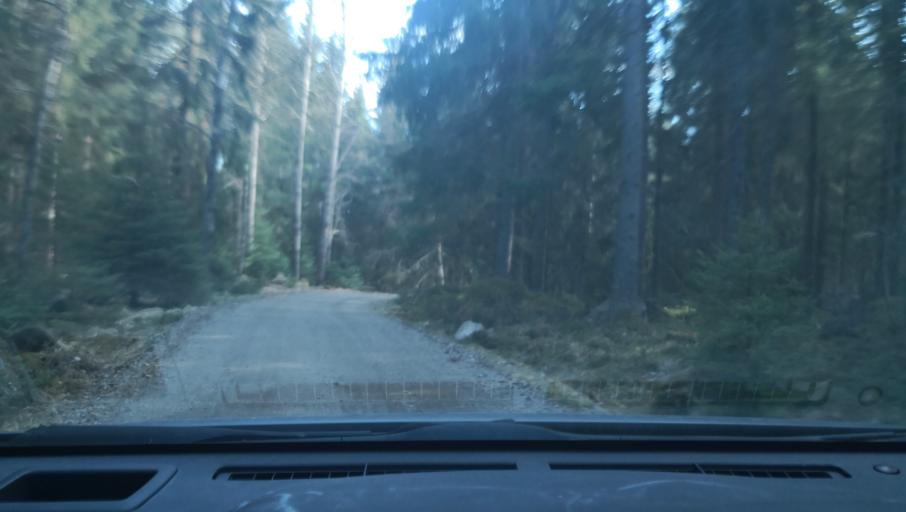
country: SE
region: Uppsala
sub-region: Heby Kommun
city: Heby
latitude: 59.8426
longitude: 16.8471
